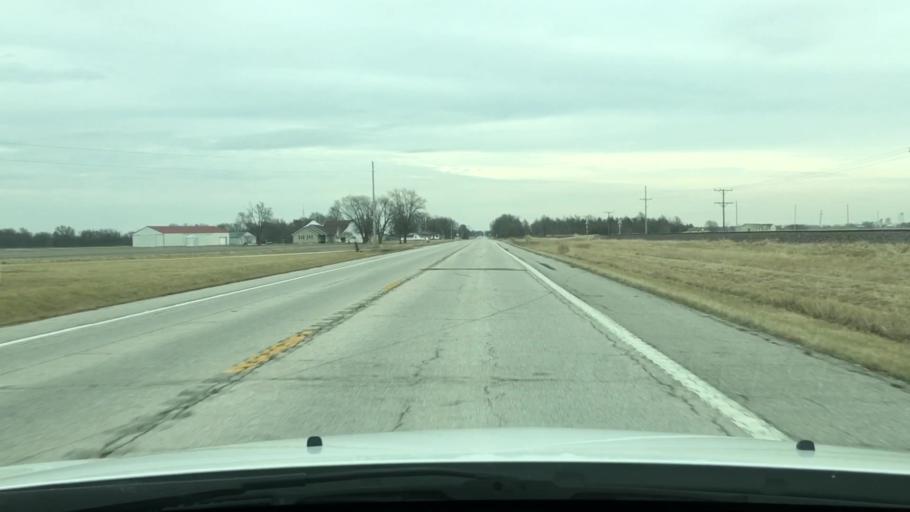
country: US
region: Missouri
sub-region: Audrain County
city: Vandalia
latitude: 39.2922
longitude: -91.5289
